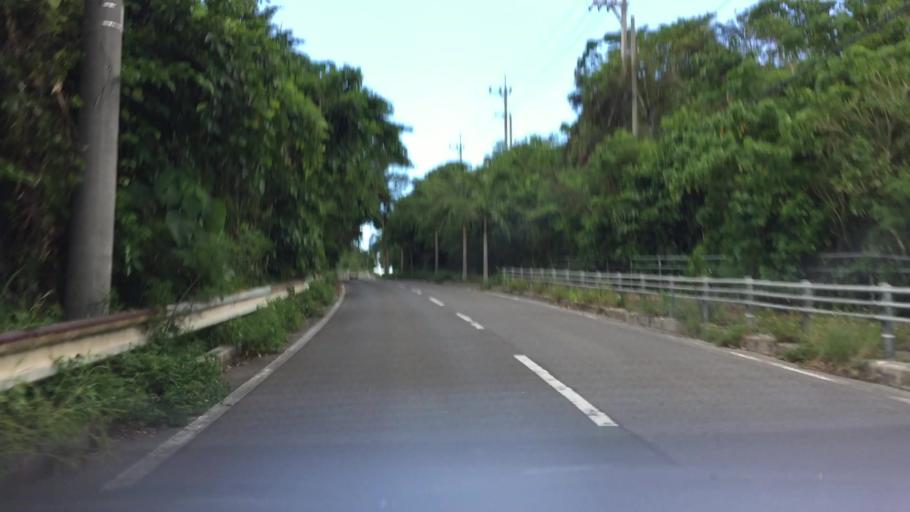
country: JP
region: Okinawa
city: Ishigaki
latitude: 24.4429
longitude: 124.1429
